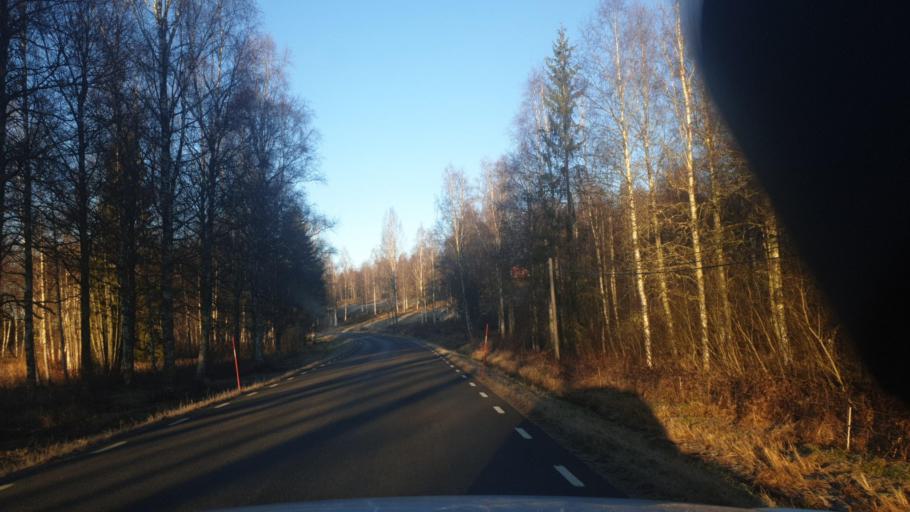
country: SE
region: Vaermland
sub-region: Eda Kommun
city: Amotfors
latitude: 59.8896
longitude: 12.5253
